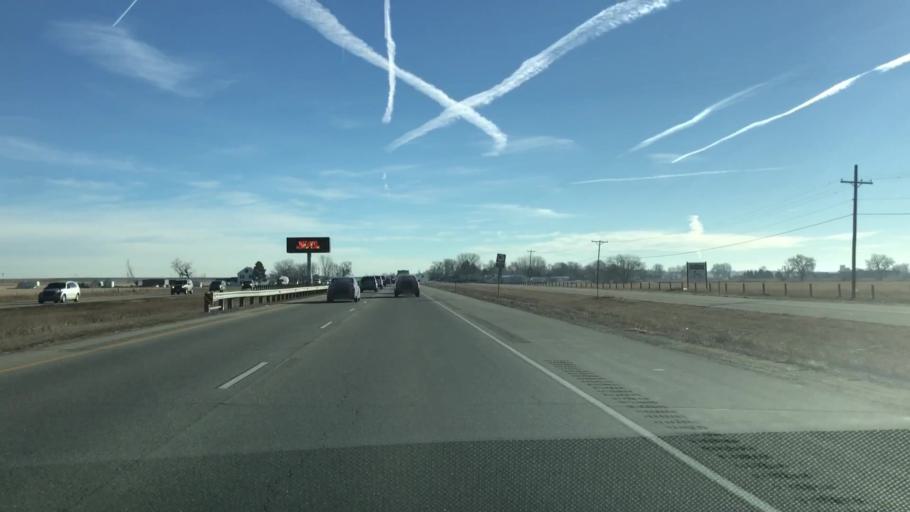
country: US
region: Colorado
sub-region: Weld County
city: Johnstown
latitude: 40.4073
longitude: -104.9610
